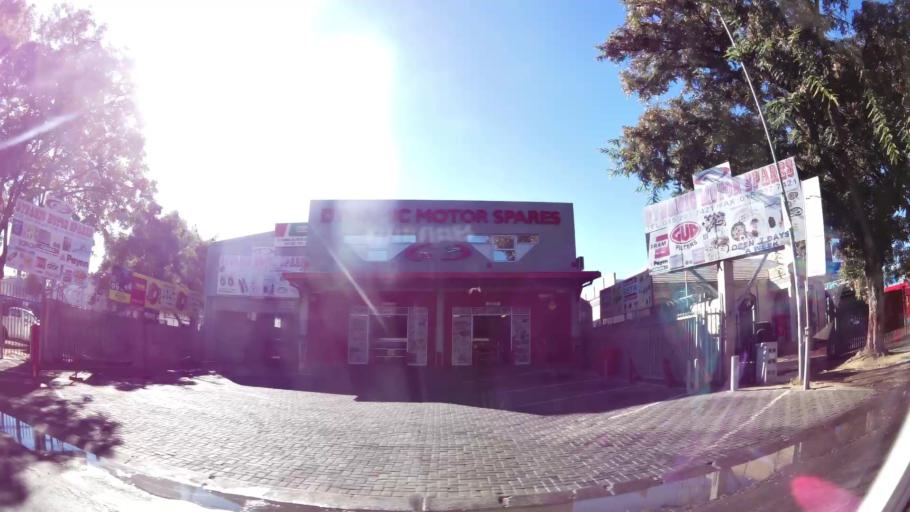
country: ZA
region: Limpopo
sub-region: Capricorn District Municipality
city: Polokwane
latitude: -23.9069
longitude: 29.4461
